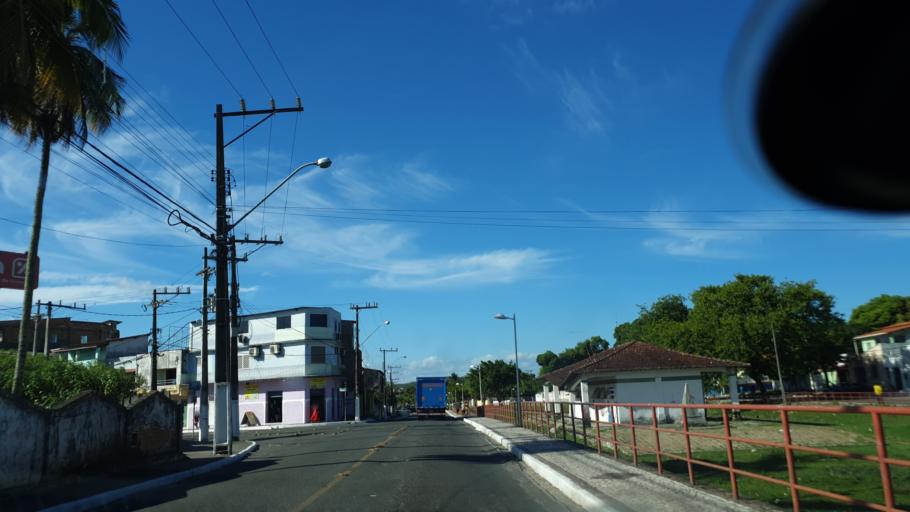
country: BR
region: Bahia
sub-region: Mata De Sao Joao
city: Mata de Sao Joao
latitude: -12.6132
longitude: -38.2974
